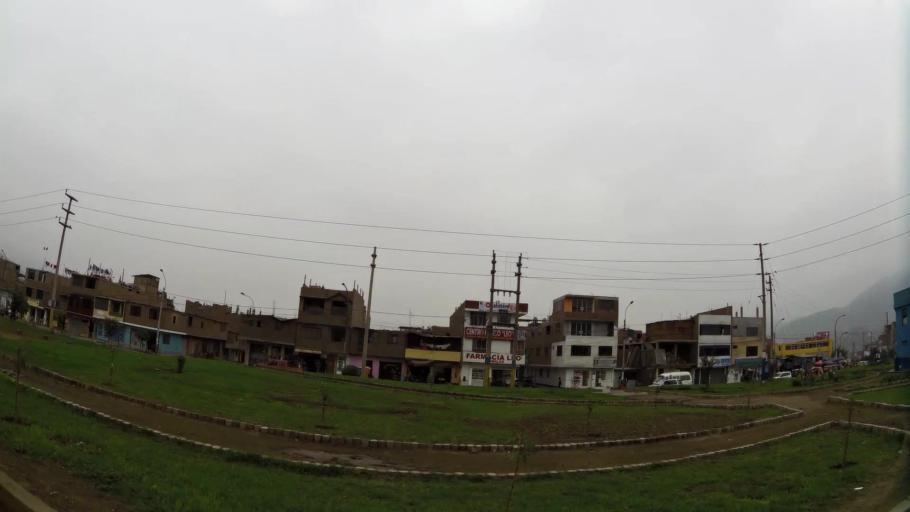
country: PE
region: Lima
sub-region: Lima
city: Independencia
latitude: -11.9558
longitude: -76.9912
